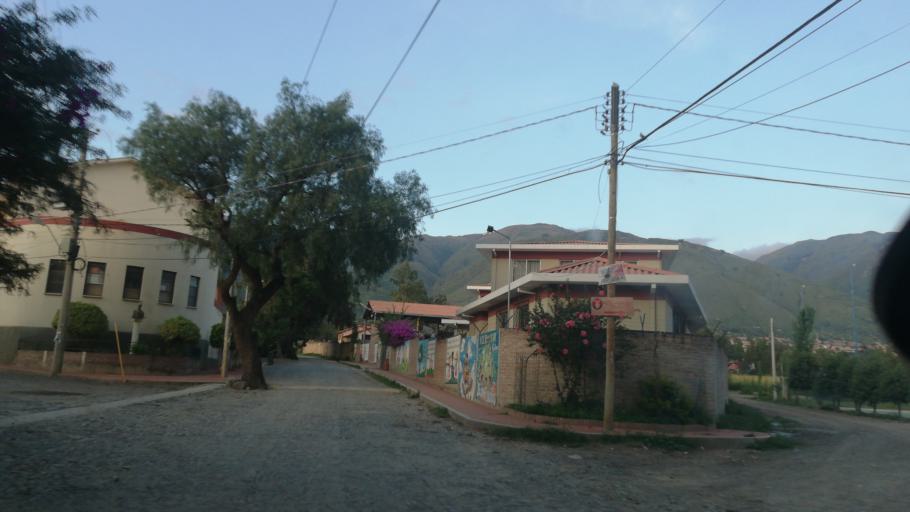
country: BO
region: Cochabamba
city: Cochabamba
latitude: -17.3415
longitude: -66.2106
